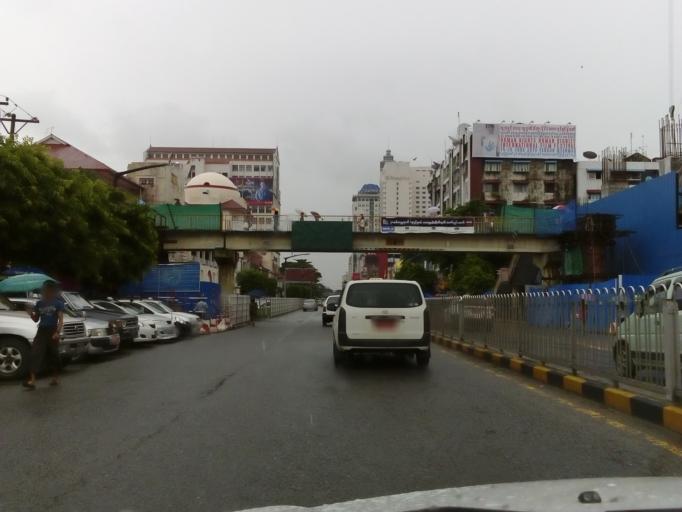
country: MM
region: Yangon
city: Yangon
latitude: 16.7795
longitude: 96.1543
